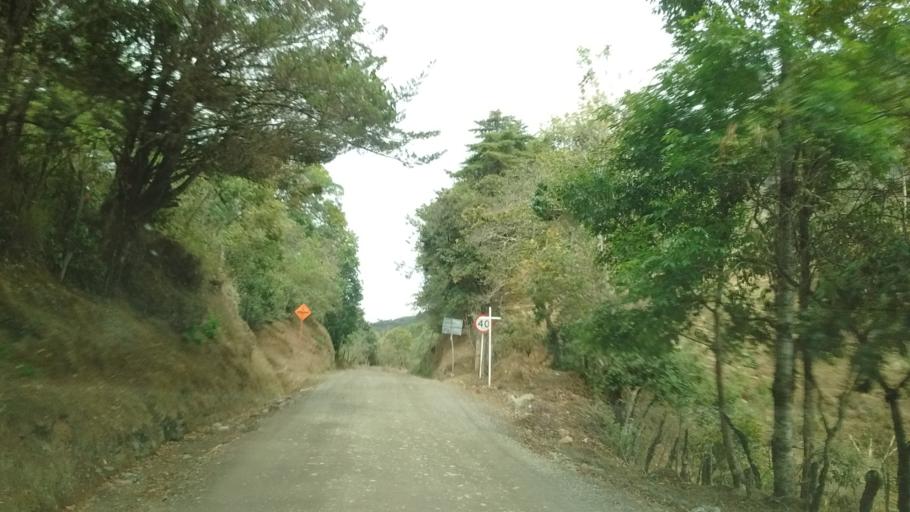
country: CO
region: Cauca
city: Almaguer
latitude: 1.8527
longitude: -76.9523
